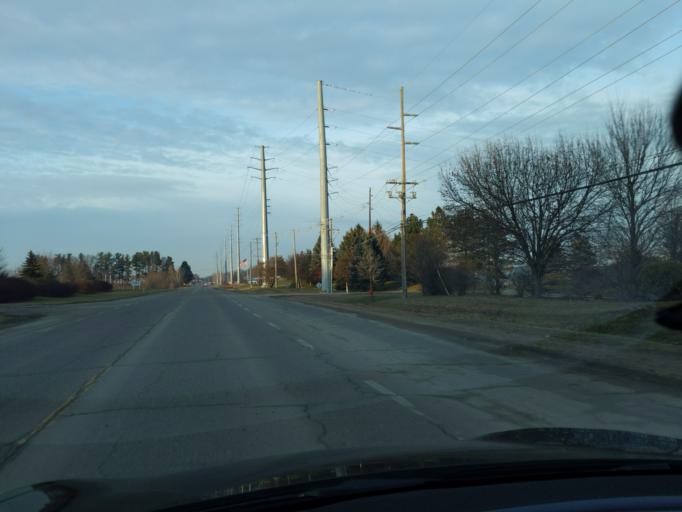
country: US
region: Michigan
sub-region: Livingston County
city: Brighton
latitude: 42.6265
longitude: -83.7525
